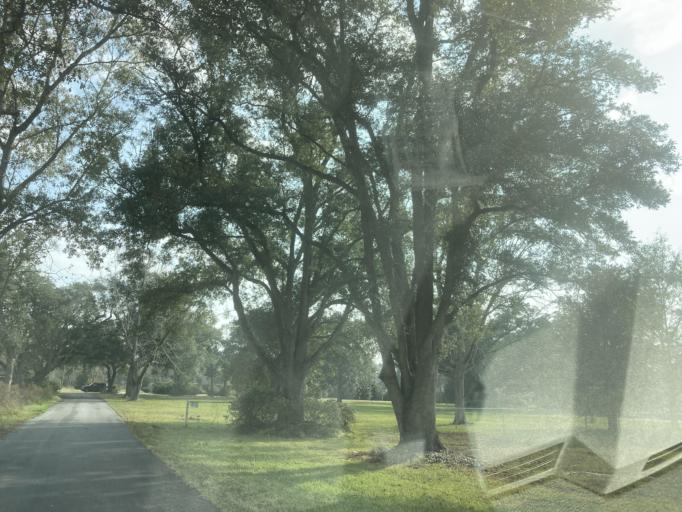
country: US
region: Mississippi
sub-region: Harrison County
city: Long Beach
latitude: 30.3559
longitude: -89.1881
